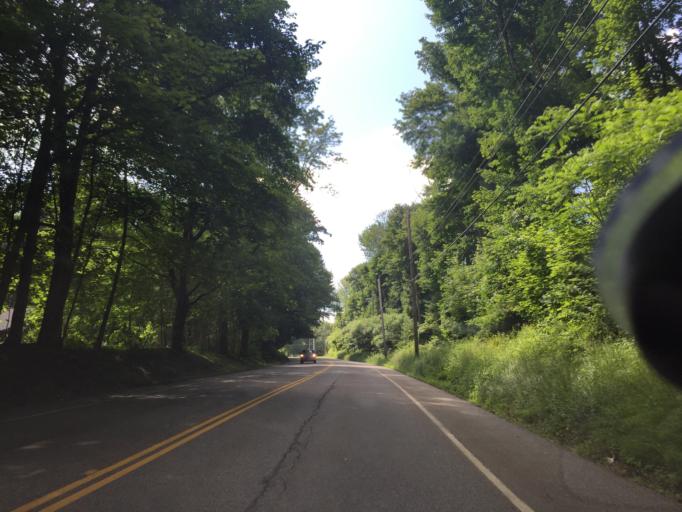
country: US
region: Connecticut
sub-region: Litchfield County
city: West Torrington
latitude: 41.8250
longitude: -73.1746
